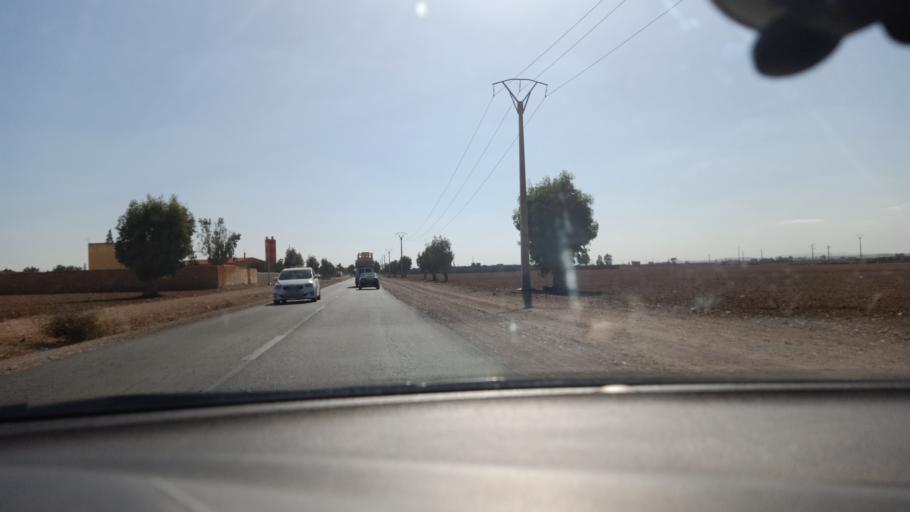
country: MA
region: Doukkala-Abda
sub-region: Safi
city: Youssoufia
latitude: 32.1043
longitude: -8.6111
